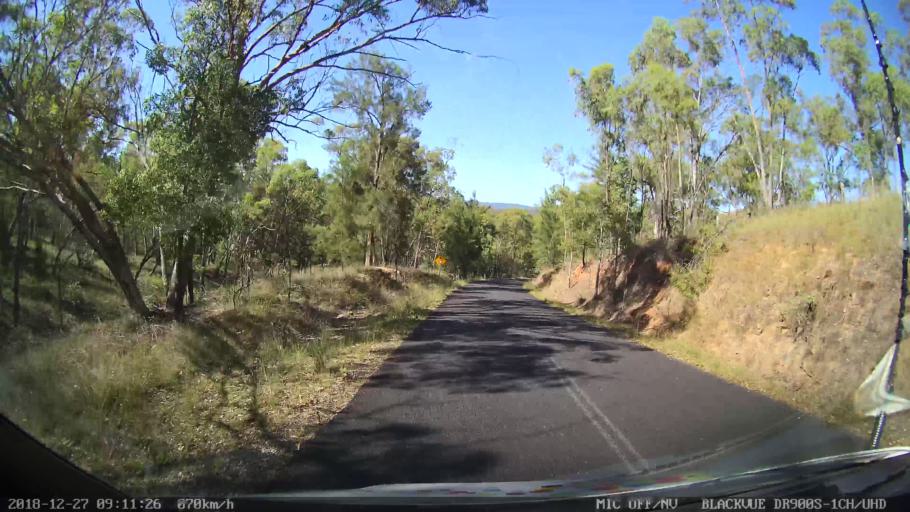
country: AU
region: New South Wales
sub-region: Lithgow
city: Portland
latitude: -33.1355
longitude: 150.1141
